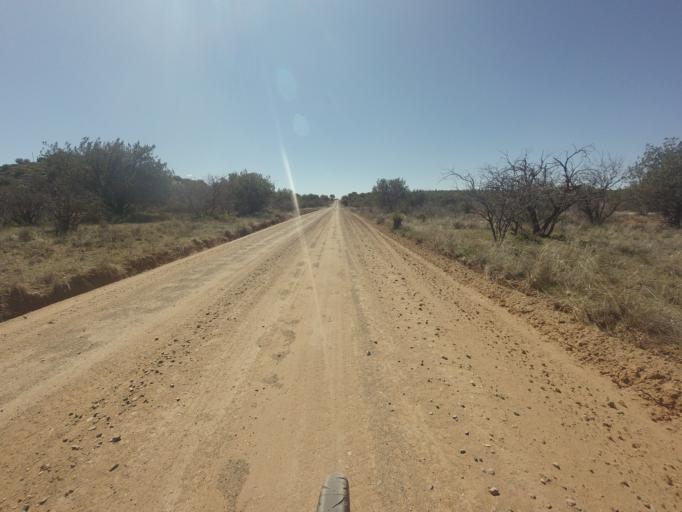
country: US
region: Arizona
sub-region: Yavapai County
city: Lake Montezuma
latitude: 34.6310
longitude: -111.7205
